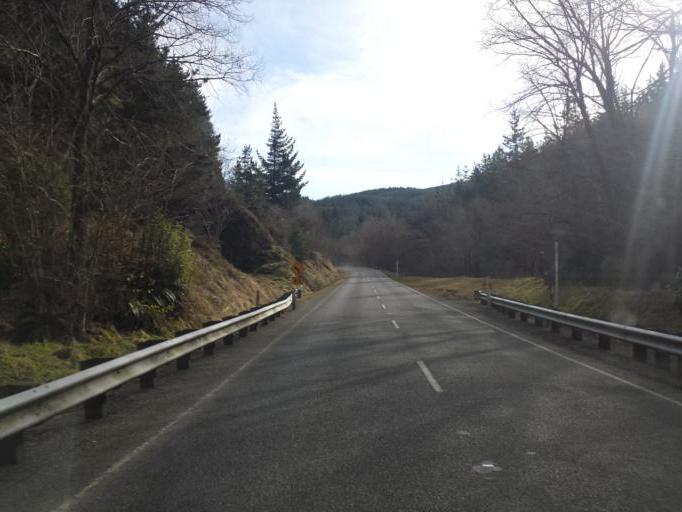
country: NZ
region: Canterbury
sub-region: Timaru District
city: Pleasant Point
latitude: -44.1272
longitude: 171.0866
